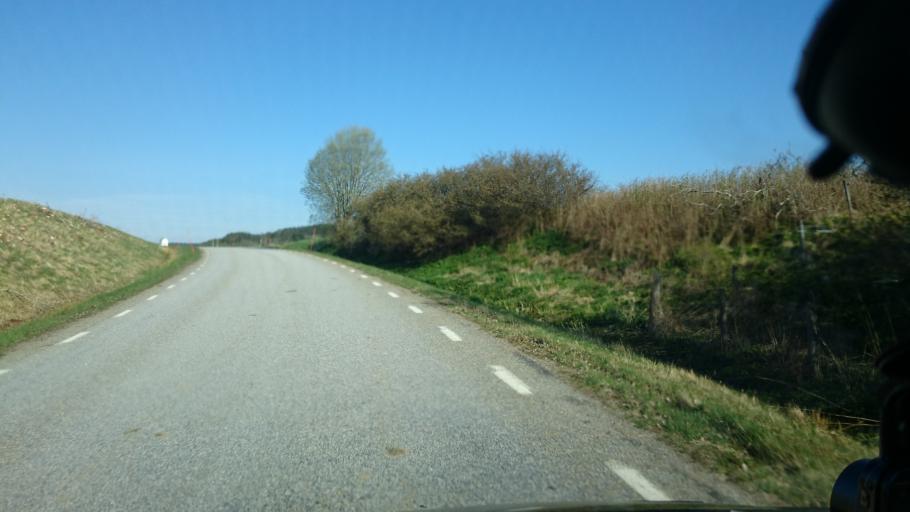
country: SE
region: Vaestra Goetaland
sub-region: Munkedals Kommun
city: Munkedal
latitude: 58.3749
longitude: 11.6830
